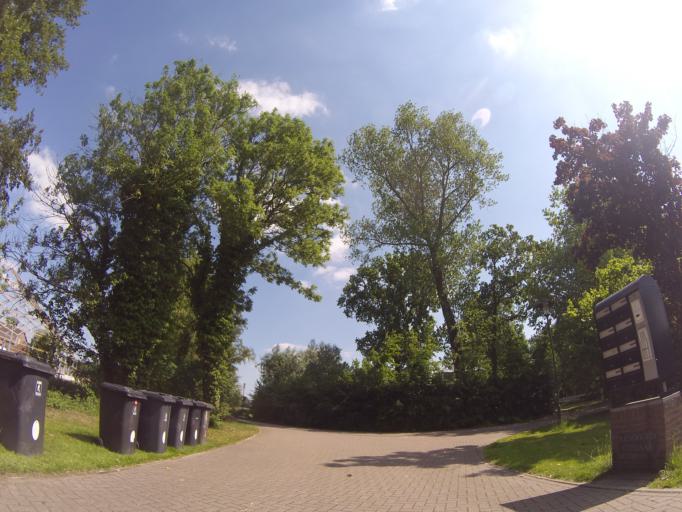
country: NL
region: Gelderland
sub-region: Gemeente Barneveld
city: Barneveld
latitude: 52.1478
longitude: 5.5589
